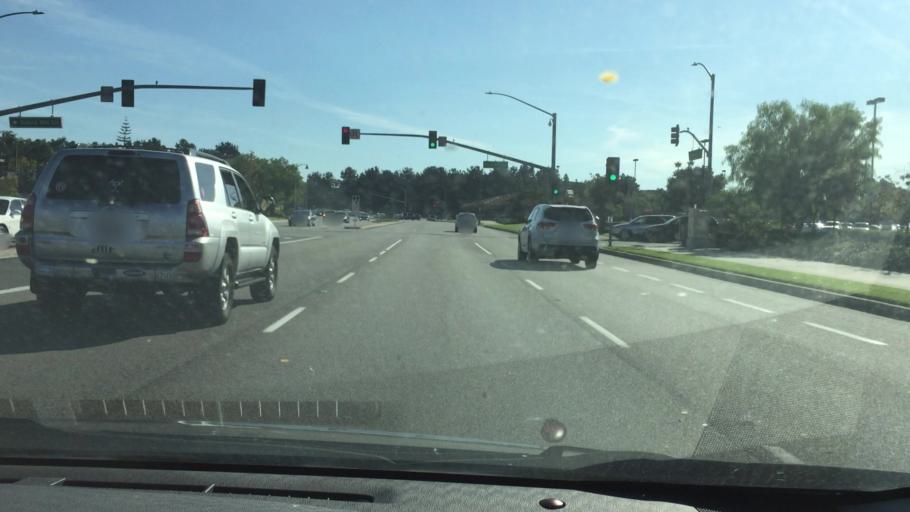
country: US
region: California
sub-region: Orange County
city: Portola Hills
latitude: 33.6531
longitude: -117.6469
